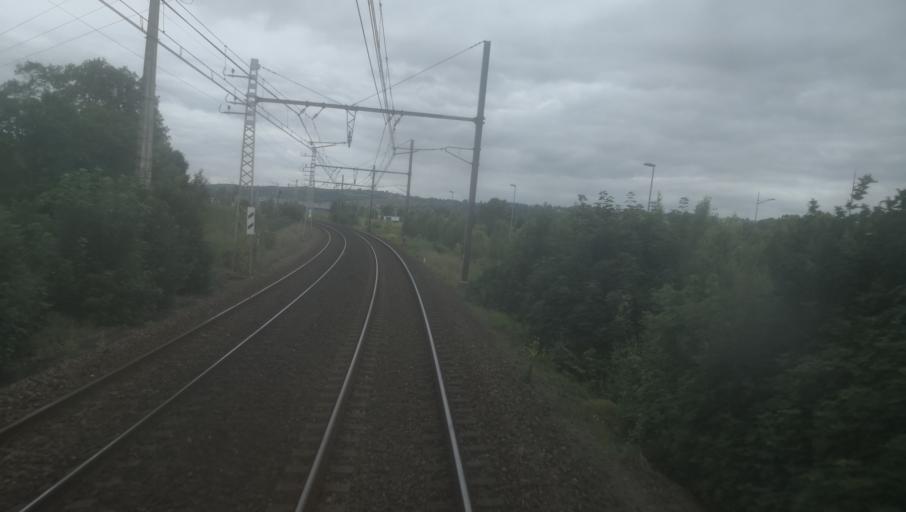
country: FR
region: Midi-Pyrenees
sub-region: Departement de la Haute-Garonne
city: Castelnau-d'Estretefonds
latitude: 43.7685
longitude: 1.3573
